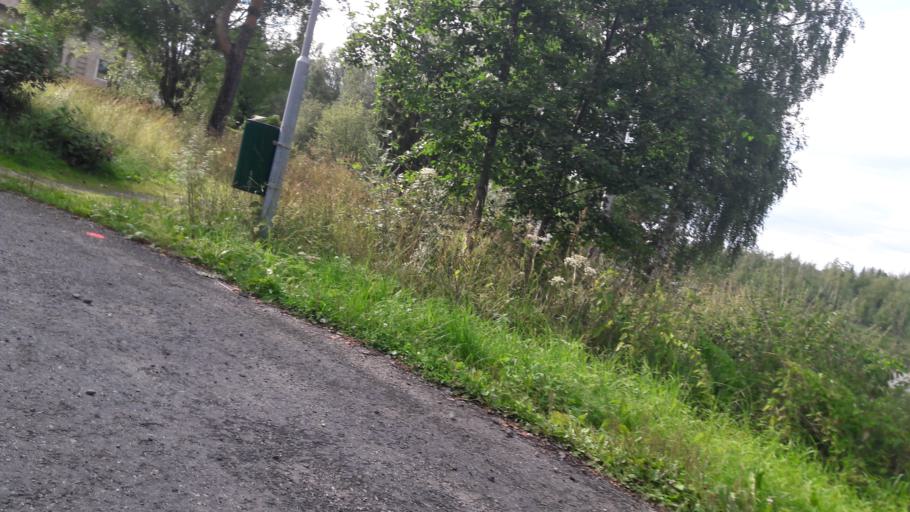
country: FI
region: North Karelia
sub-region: Joensuu
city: Joensuu
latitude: 62.5989
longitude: 29.7901
